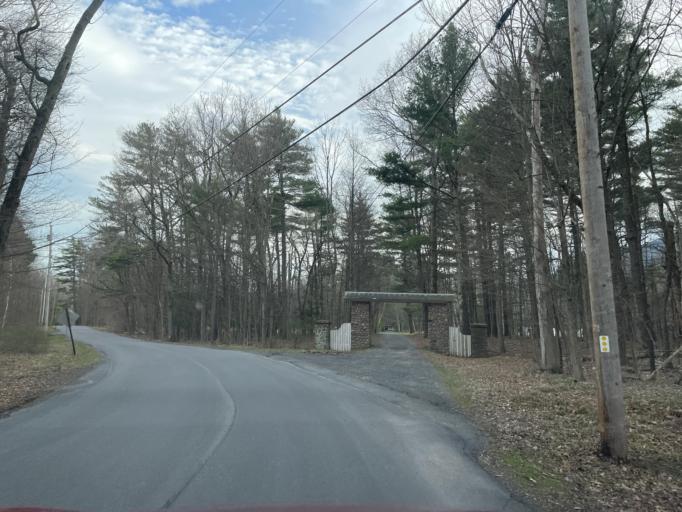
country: US
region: New York
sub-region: Greene County
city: Palenville
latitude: 42.1681
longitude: -74.0220
